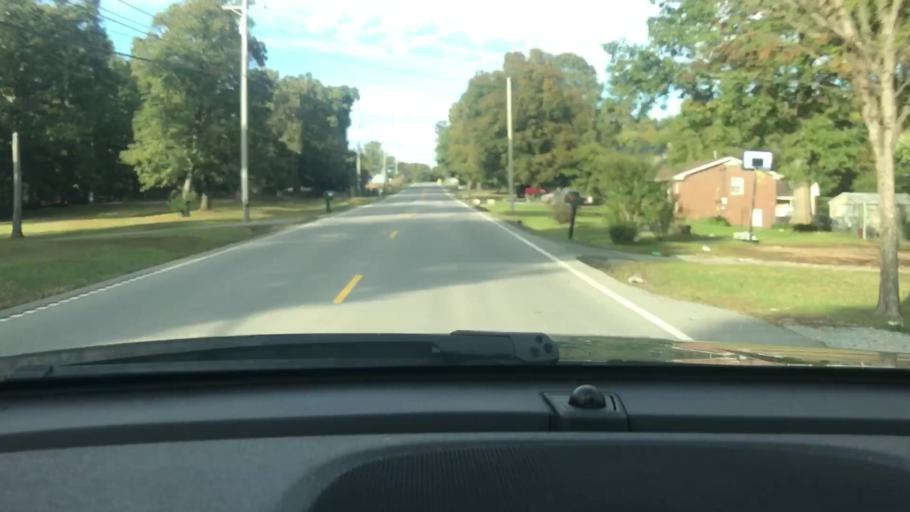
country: US
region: Tennessee
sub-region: Dickson County
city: White Bluff
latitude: 36.1442
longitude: -87.2344
